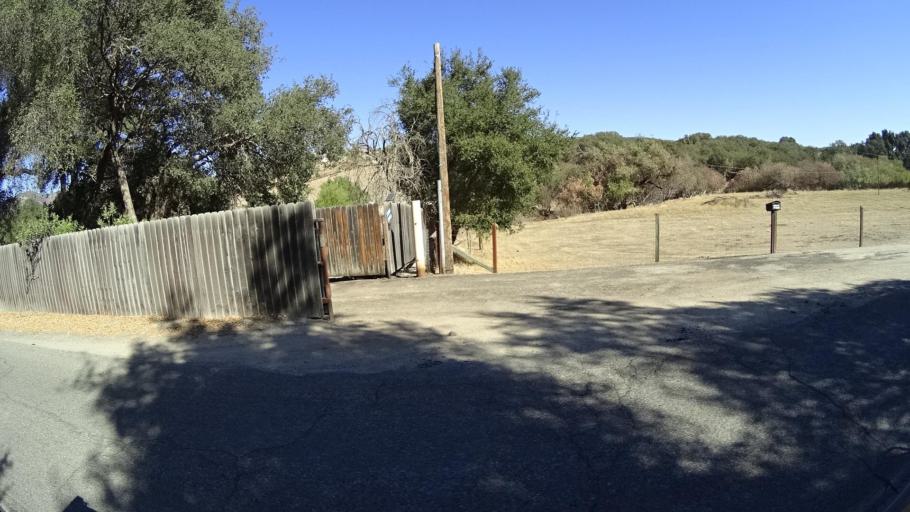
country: US
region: California
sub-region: Monterey County
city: King City
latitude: 36.1511
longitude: -121.1875
